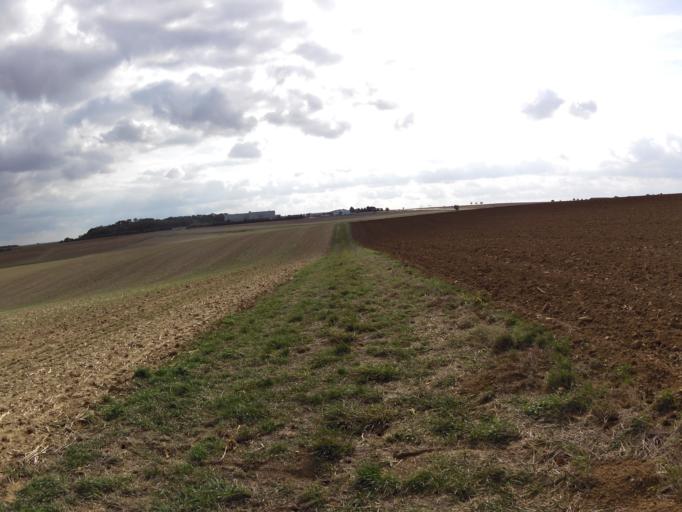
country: DE
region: Bavaria
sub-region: Regierungsbezirk Unterfranken
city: Reichenberg
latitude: 49.7015
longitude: 9.9421
